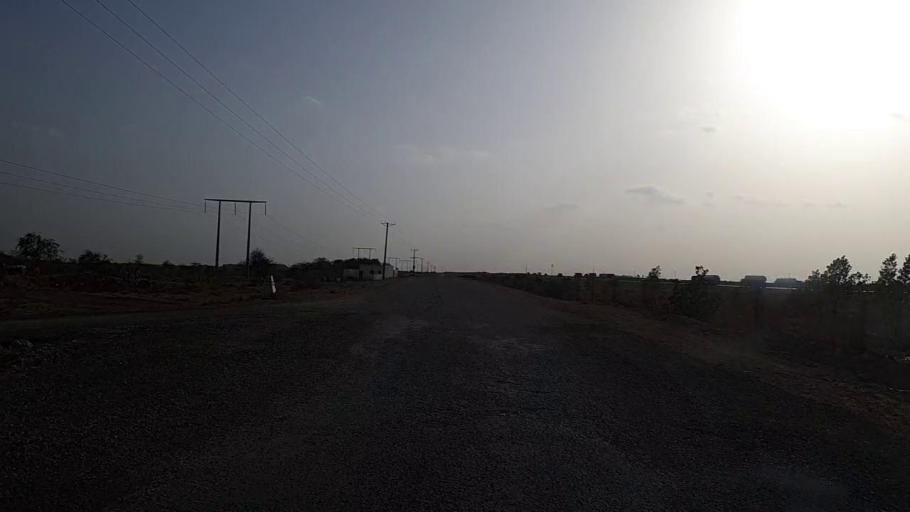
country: PK
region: Sindh
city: Thatta
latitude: 25.1943
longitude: 67.8638
